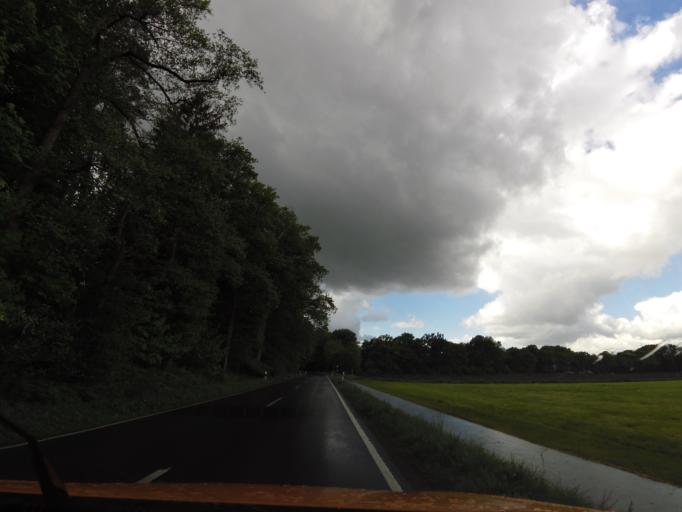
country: DE
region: Lower Saxony
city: Hude
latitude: 53.1220
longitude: 8.4325
